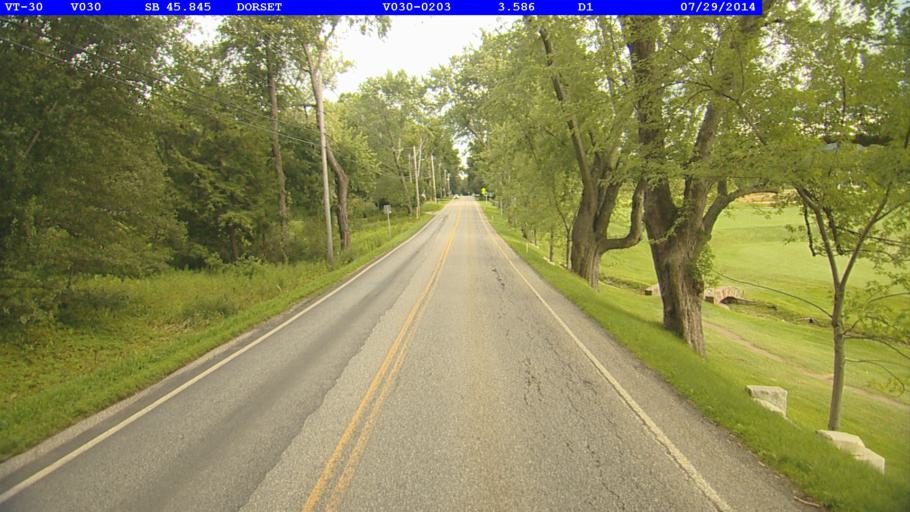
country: US
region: Vermont
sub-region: Bennington County
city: Manchester Center
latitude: 43.2574
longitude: -73.1012
